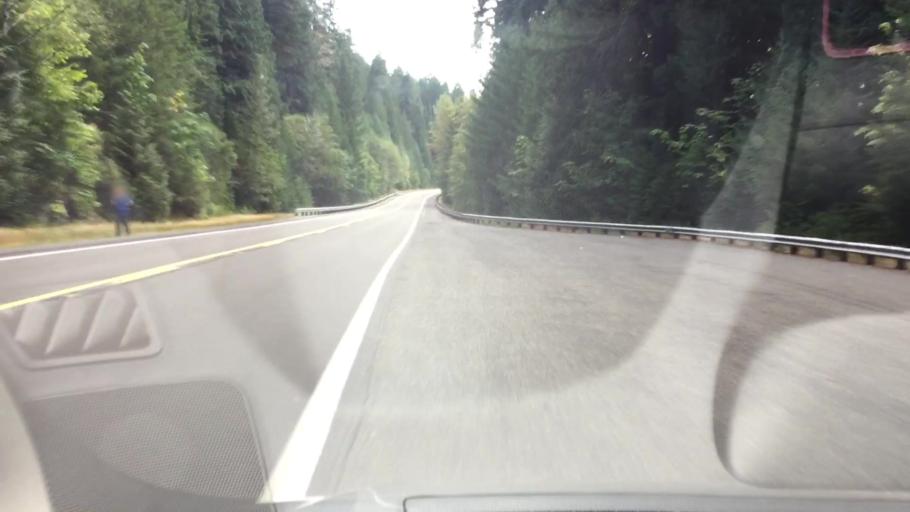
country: US
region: Washington
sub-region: Pierce County
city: Buckley
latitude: 46.6541
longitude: -121.6035
